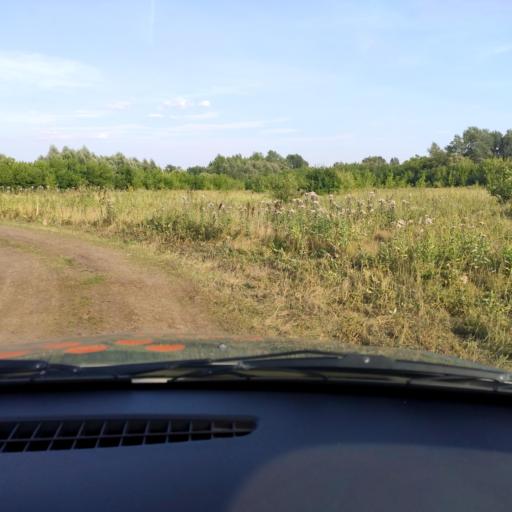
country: RU
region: Bashkortostan
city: Ufa
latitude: 54.6085
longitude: 55.9641
